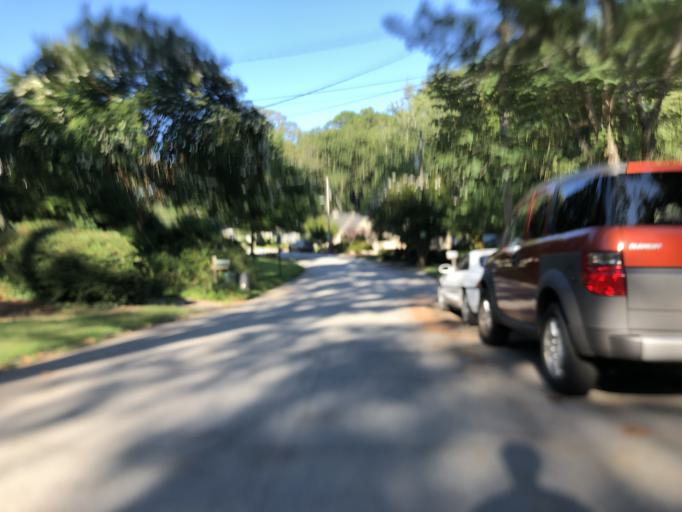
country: US
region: Georgia
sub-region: DeKalb County
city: North Decatur
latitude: 33.7891
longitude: -84.3115
